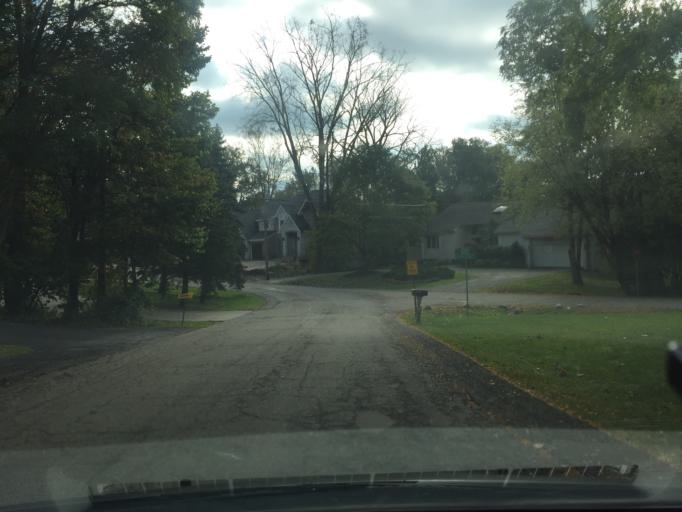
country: US
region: Michigan
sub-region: Oakland County
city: Sylvan Lake
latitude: 42.5930
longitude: -83.3260
